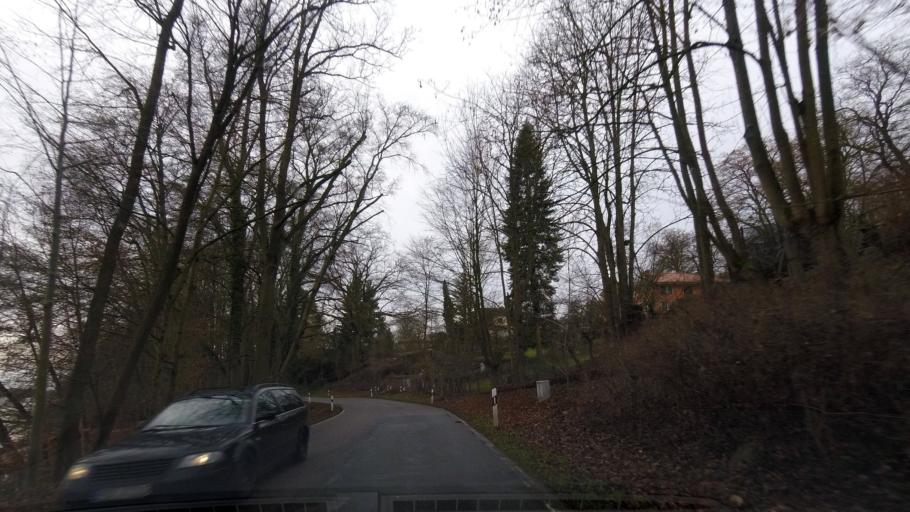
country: DE
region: Mecklenburg-Vorpommern
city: Waren
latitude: 53.5391
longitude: 12.6874
